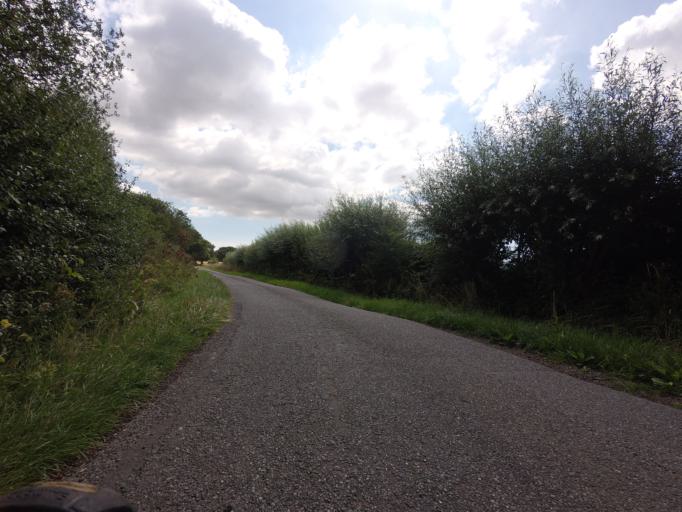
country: GB
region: England
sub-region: Kent
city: Stone
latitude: 51.0531
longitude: 0.7687
